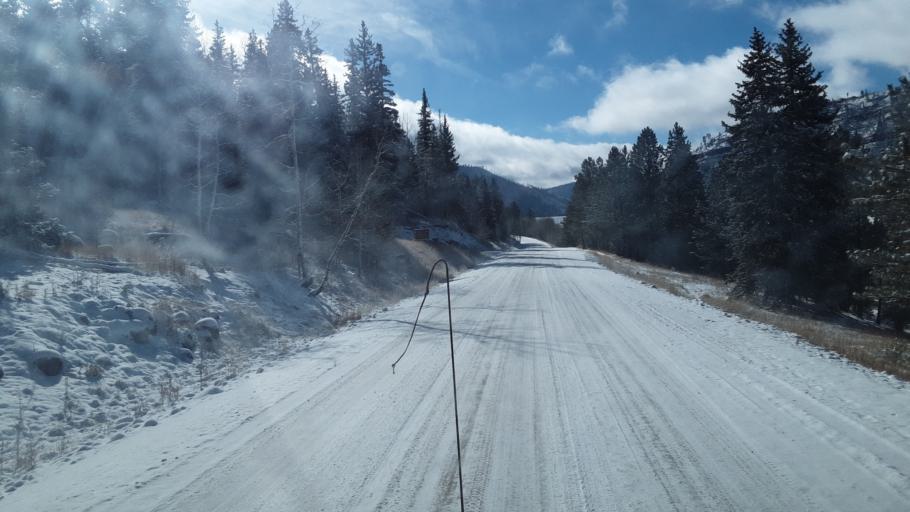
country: US
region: Colorado
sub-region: La Plata County
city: Bayfield
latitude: 37.4036
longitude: -107.6594
